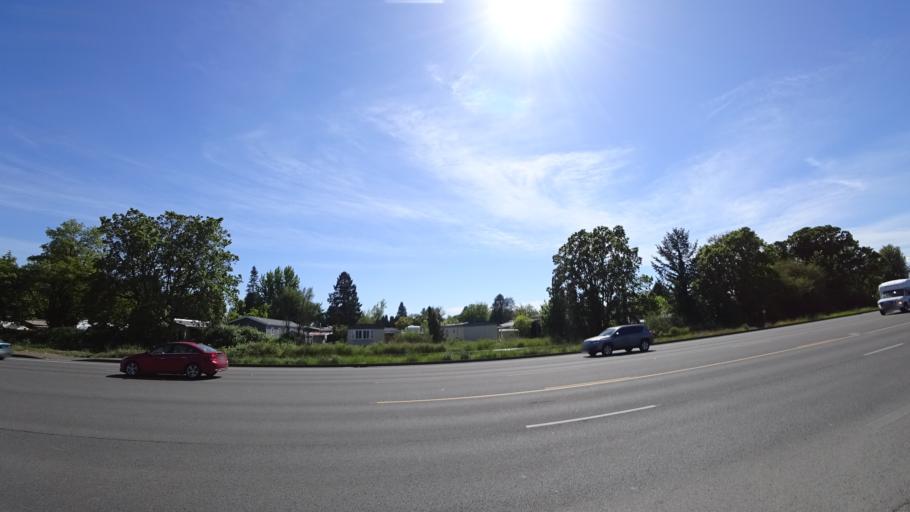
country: US
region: Oregon
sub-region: Washington County
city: Hillsboro
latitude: 45.5083
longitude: -122.9645
